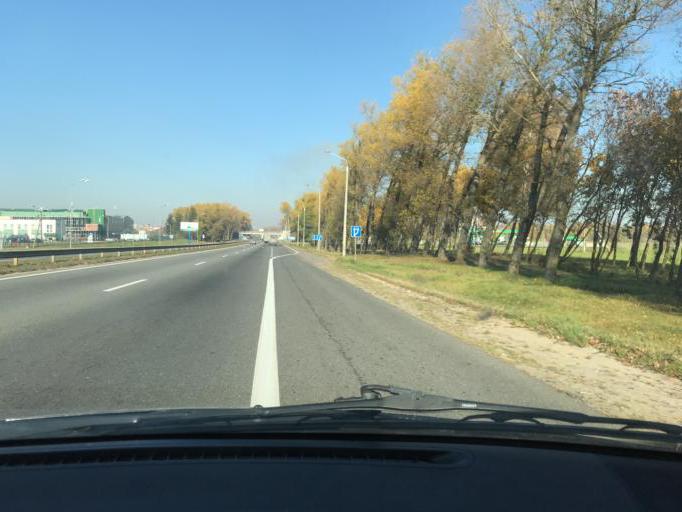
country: BY
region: Minsk
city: Yubilyeyny
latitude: 53.8094
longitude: 27.5297
